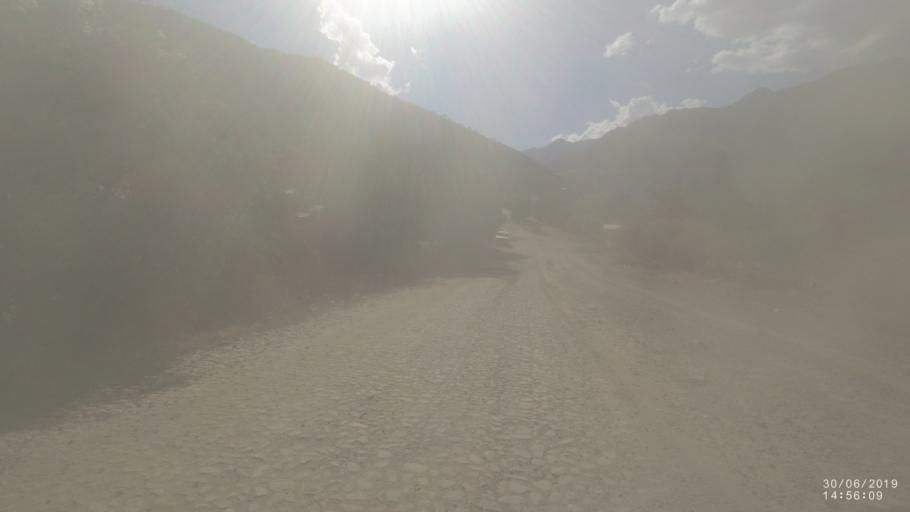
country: BO
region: Cochabamba
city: Irpa Irpa
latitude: -17.7507
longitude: -66.3527
